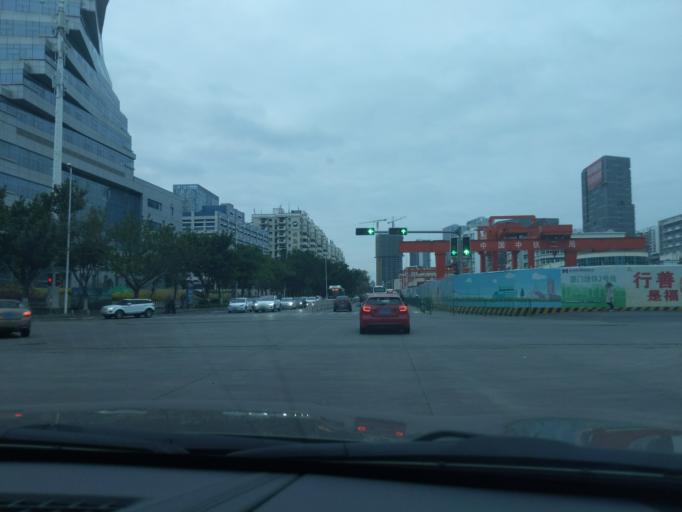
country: CN
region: Fujian
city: Liuwudian
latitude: 24.4848
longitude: 118.1755
